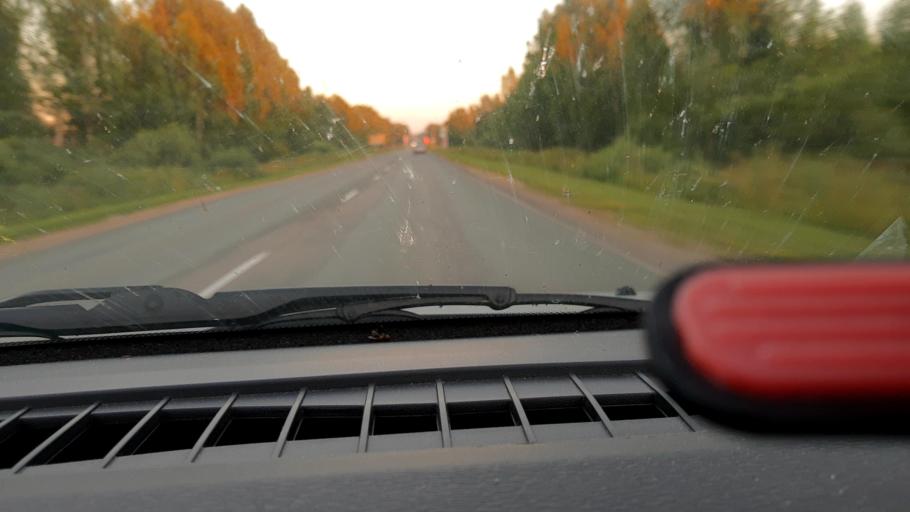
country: RU
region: Nizjnij Novgorod
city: Sharanga
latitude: 57.1996
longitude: 46.5244
